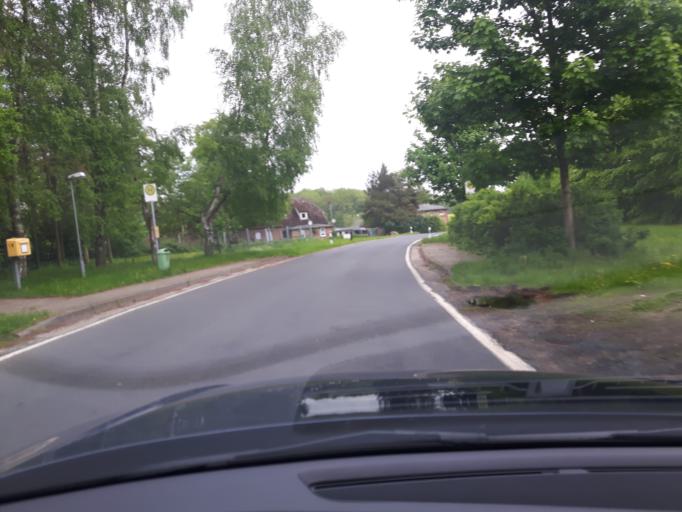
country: DE
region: Mecklenburg-Vorpommern
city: Velgast
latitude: 54.2023
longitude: 12.7294
